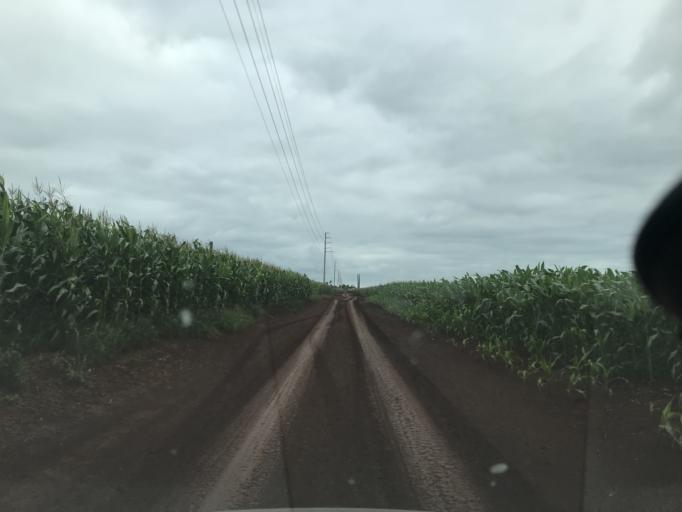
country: BR
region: Parana
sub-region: Palotina
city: Palotina
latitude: -24.3043
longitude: -53.8212
